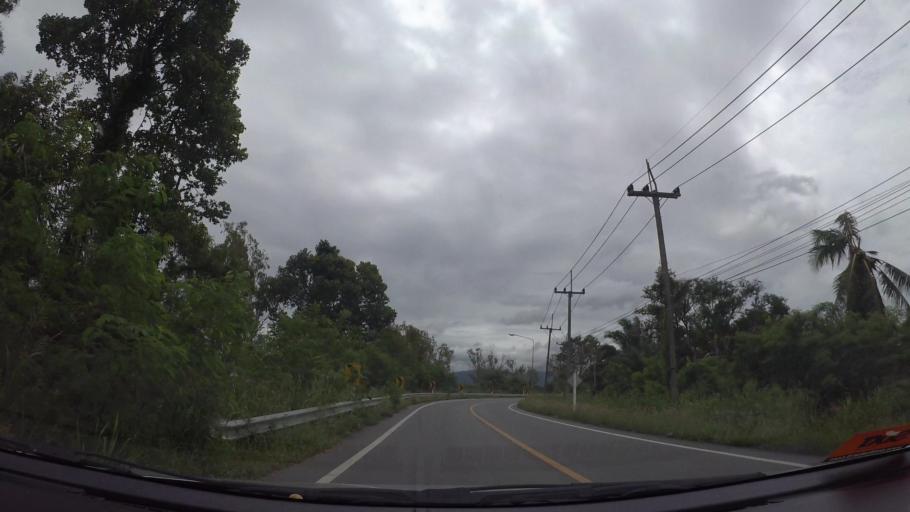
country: TH
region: Chon Buri
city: Si Racha
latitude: 13.1831
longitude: 100.9689
